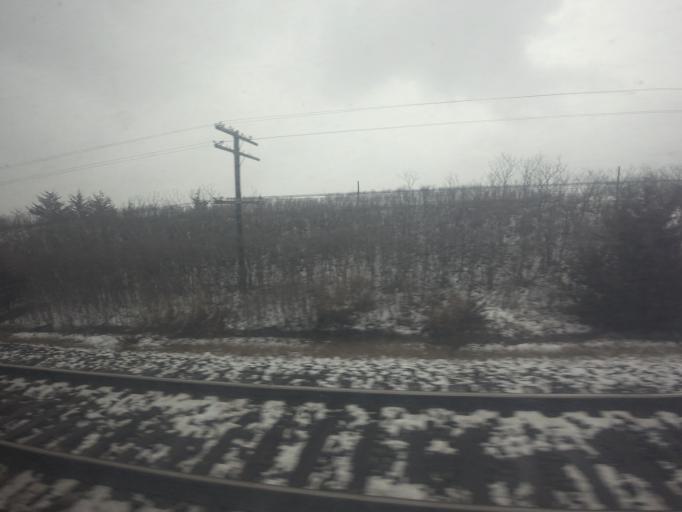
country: CA
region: Ontario
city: Quinte West
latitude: 44.0958
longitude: -77.6219
